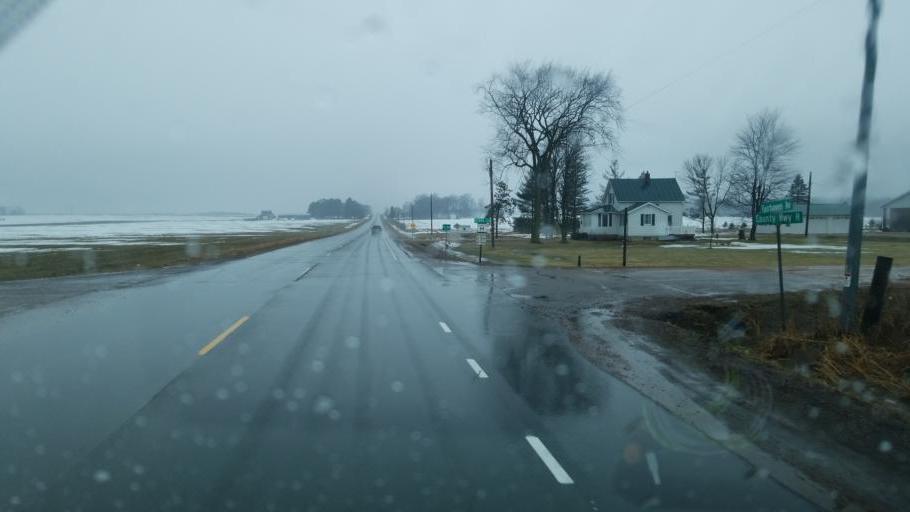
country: US
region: Wisconsin
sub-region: Marathon County
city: Spencer
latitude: 44.6561
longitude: -90.3162
